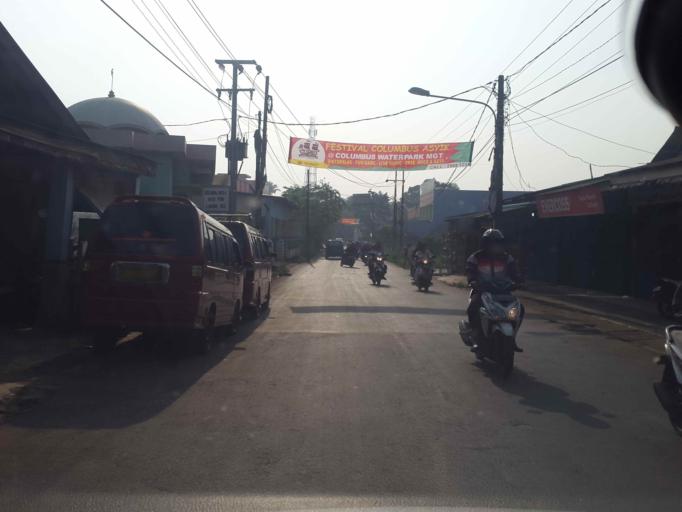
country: ID
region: West Java
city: Bekasi
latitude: -6.3135
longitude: 106.9913
